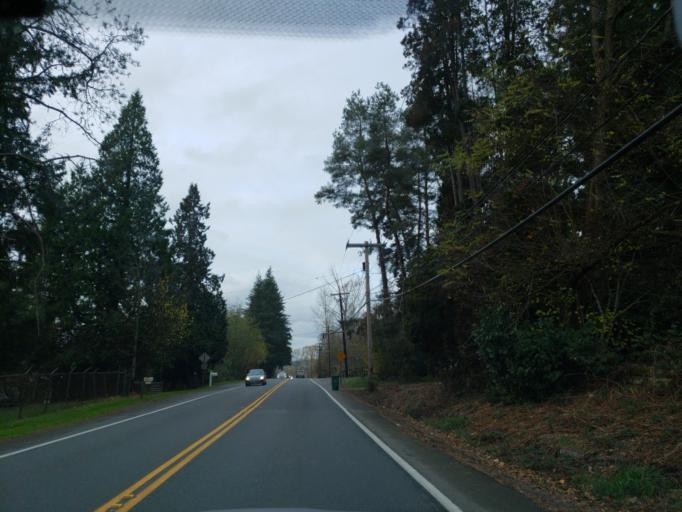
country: US
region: Washington
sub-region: King County
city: Woodinville
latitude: 47.7396
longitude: -122.1428
